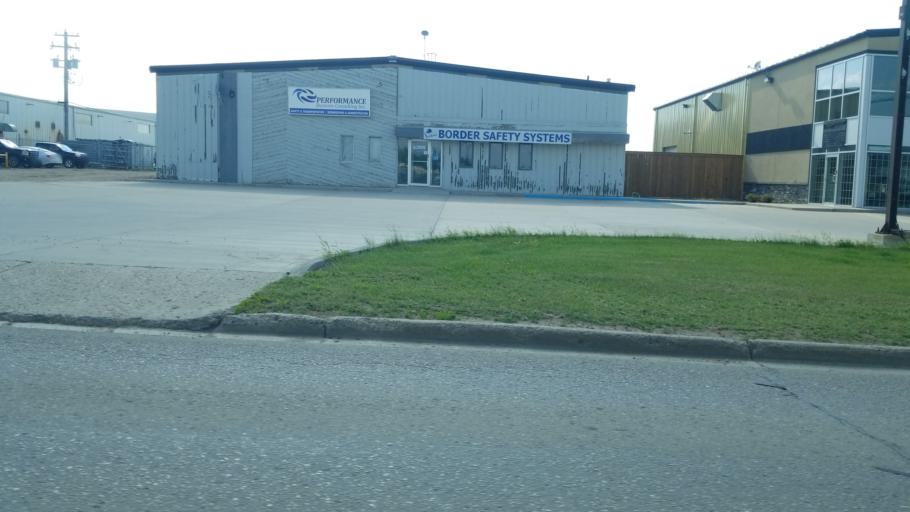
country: CA
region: Saskatchewan
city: Lloydminster
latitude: 53.2811
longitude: -110.0340
